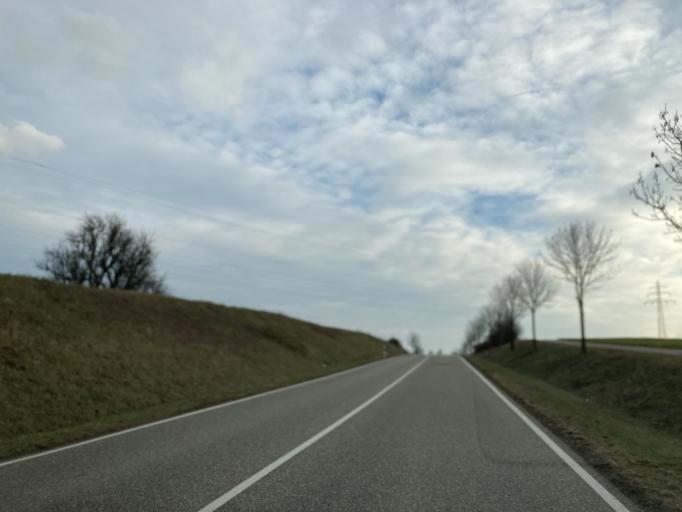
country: DE
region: Baden-Wuerttemberg
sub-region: Karlsruhe Region
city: Oberderdingen
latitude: 49.0689
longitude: 8.7888
